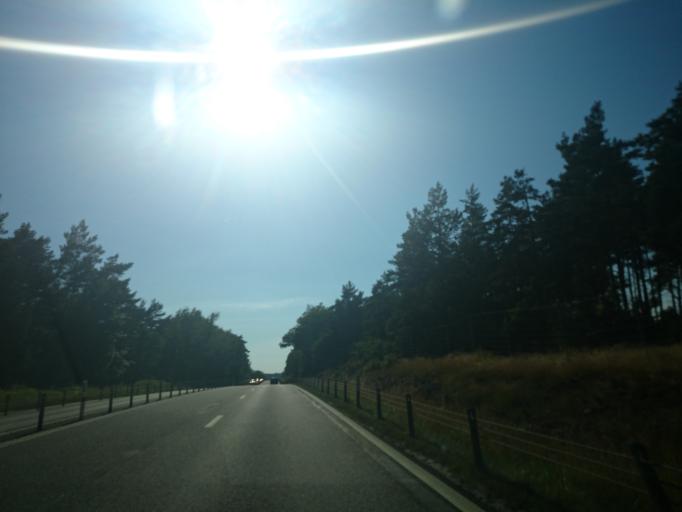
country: SE
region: Blekinge
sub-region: Karlskrona Kommun
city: Nattraby
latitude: 56.1972
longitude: 15.4597
